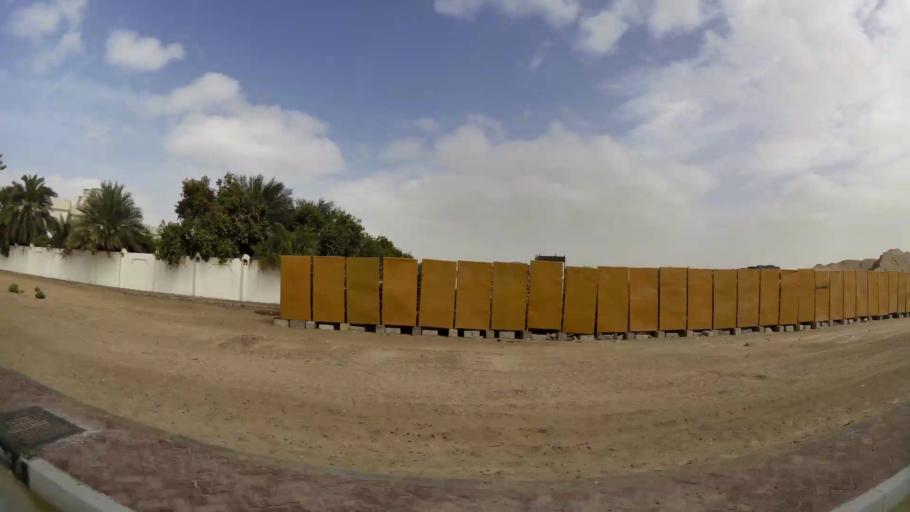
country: AE
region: Abu Dhabi
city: Abu Dhabi
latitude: 24.4005
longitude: 54.5084
